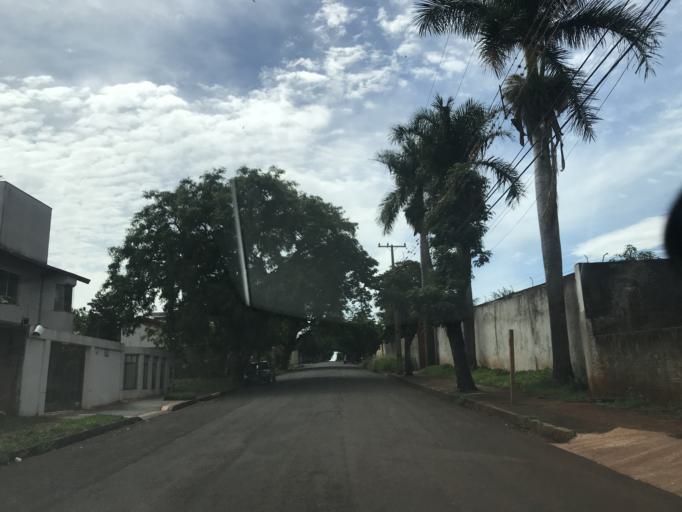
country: BR
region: Parana
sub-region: Londrina
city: Londrina
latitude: -23.3461
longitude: -51.1623
